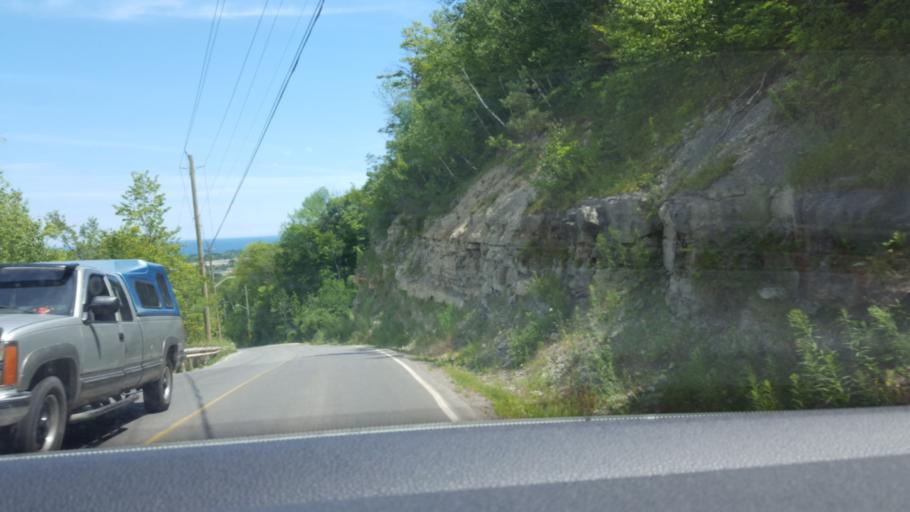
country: CA
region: Ontario
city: Hamilton
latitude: 43.1916
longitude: -79.5979
